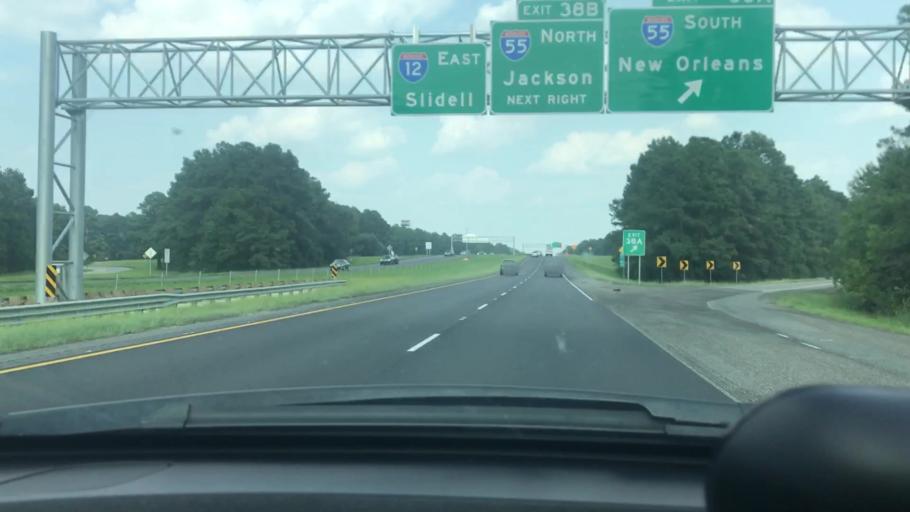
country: US
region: Louisiana
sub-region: Tangipahoa Parish
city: Hammond
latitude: 30.4789
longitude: -90.4939
